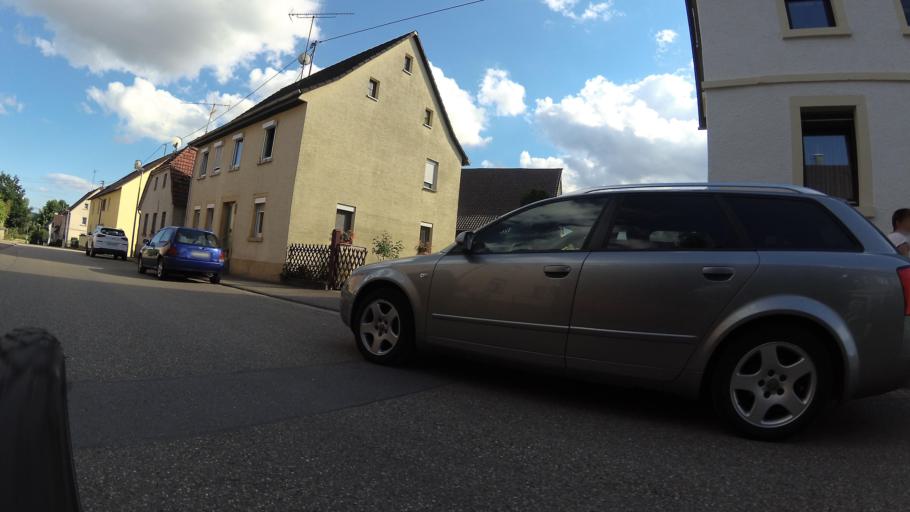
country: DE
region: Baden-Wuerttemberg
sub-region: Regierungsbezirk Stuttgart
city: Neuenstadt am Kocher
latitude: 49.2447
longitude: 9.3101
